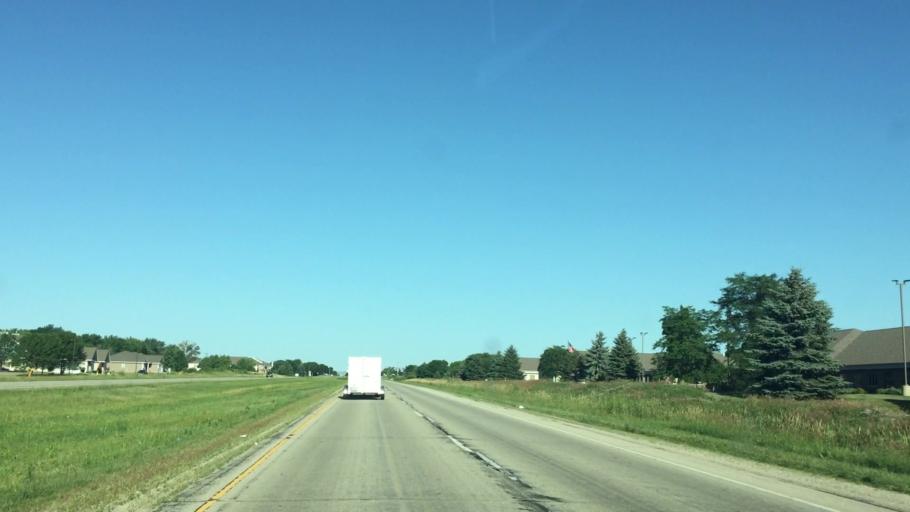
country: US
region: Wisconsin
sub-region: Outagamie County
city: Appleton
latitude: 44.2623
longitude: -88.4879
